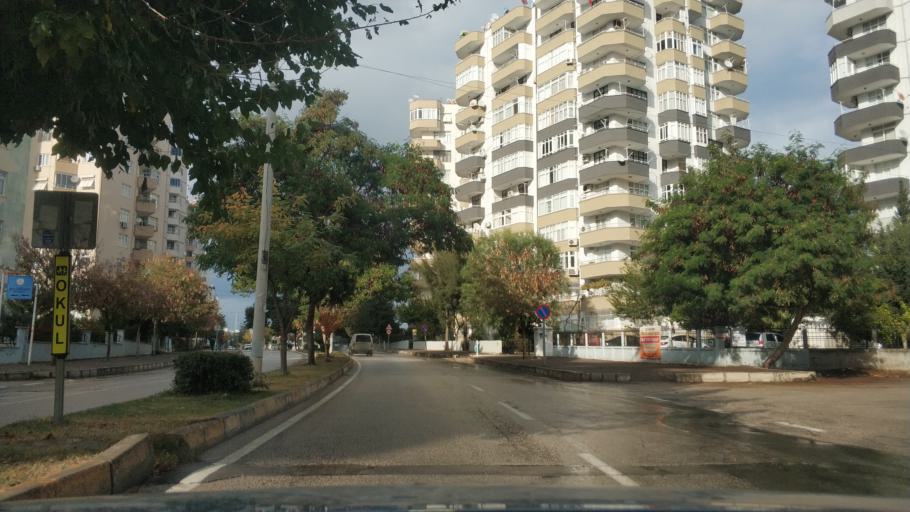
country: TR
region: Adana
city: Seyhan
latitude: 37.0370
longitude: 35.2615
